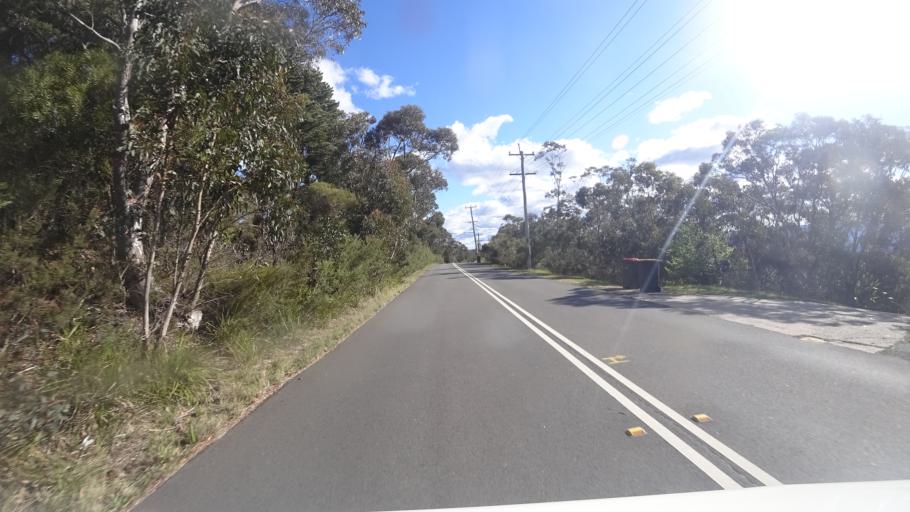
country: AU
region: New South Wales
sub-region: Blue Mountains Municipality
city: Katoomba
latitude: -33.7172
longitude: 150.2957
